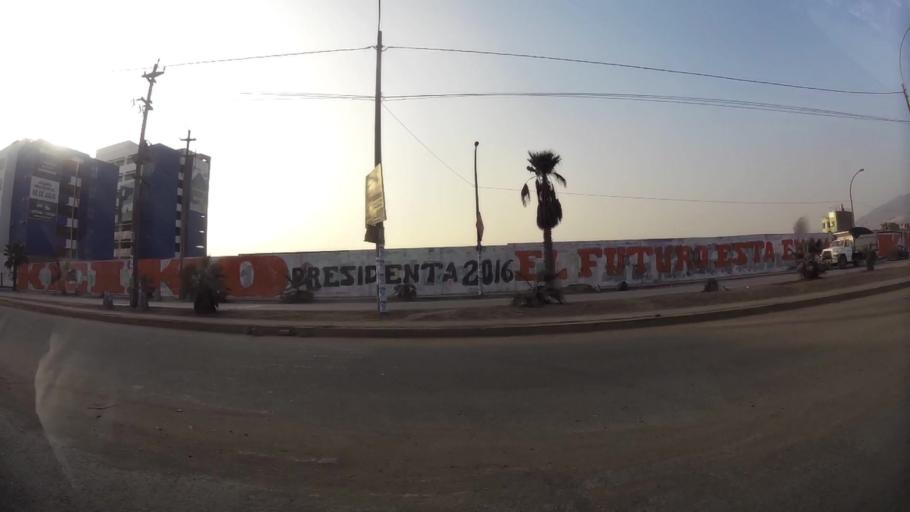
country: PE
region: Lima
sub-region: Lima
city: Independencia
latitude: -11.9617
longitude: -77.0644
